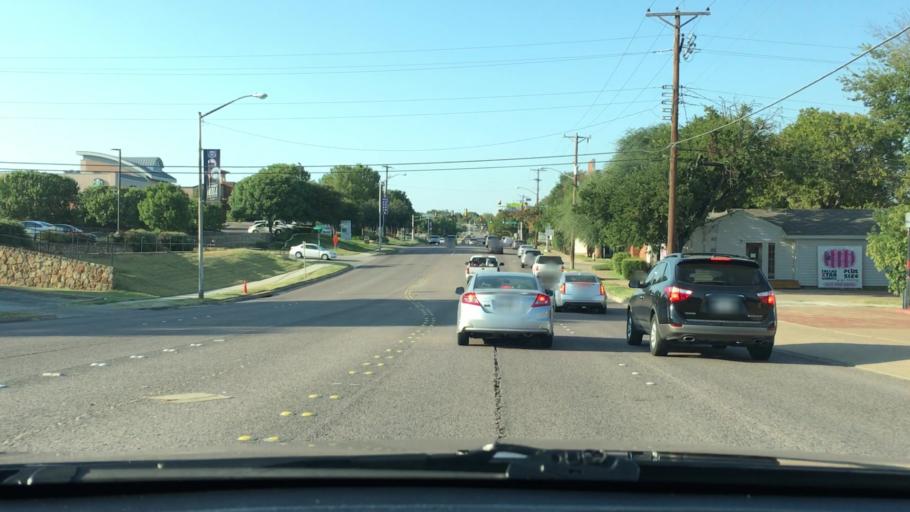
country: US
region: Texas
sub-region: Tarrant County
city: Westworth
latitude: 32.7273
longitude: -97.3878
